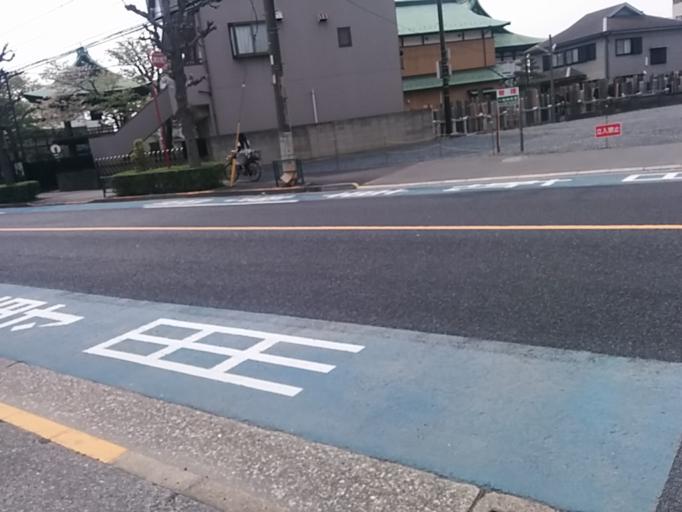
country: JP
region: Tokyo
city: Urayasu
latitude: 35.6777
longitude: 139.8605
